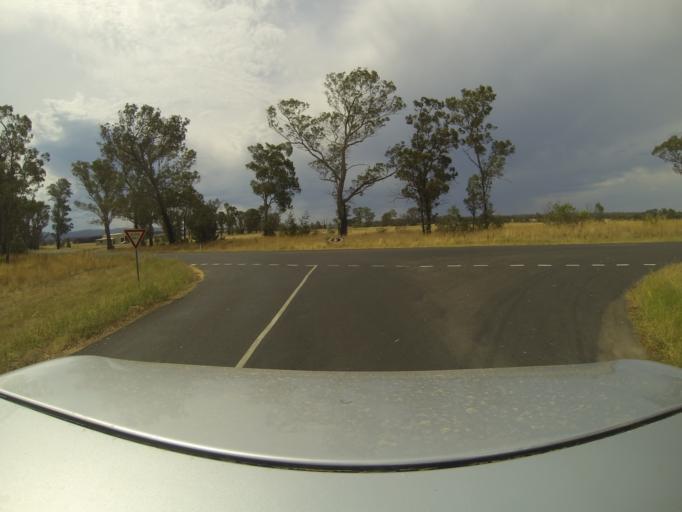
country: AU
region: Victoria
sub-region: Wellington
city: Heyfield
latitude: -37.9419
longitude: 146.6996
